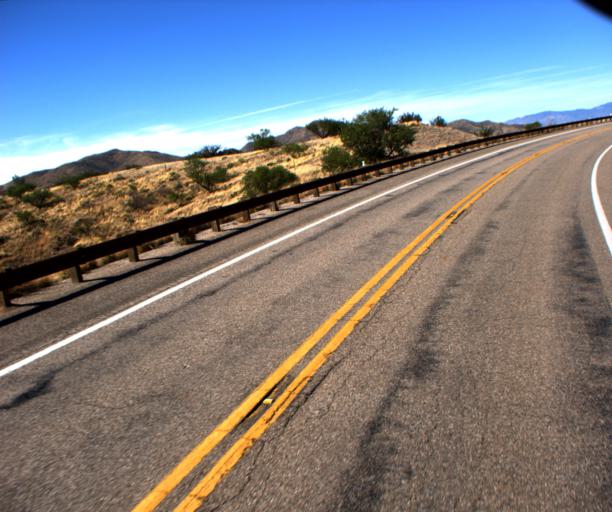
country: US
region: Arizona
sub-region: Pima County
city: Corona de Tucson
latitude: 31.8293
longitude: -110.7138
